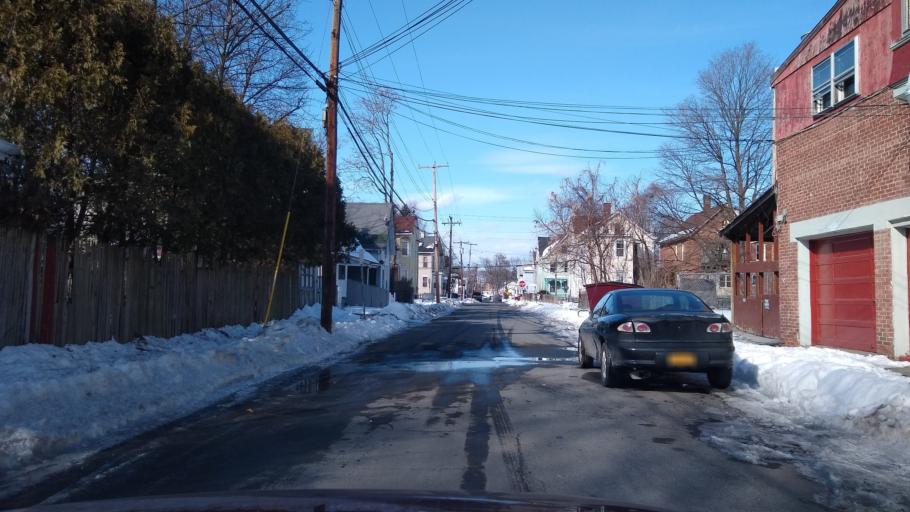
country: US
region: New York
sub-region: Ulster County
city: Kingston
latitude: 41.9275
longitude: -74.0082
